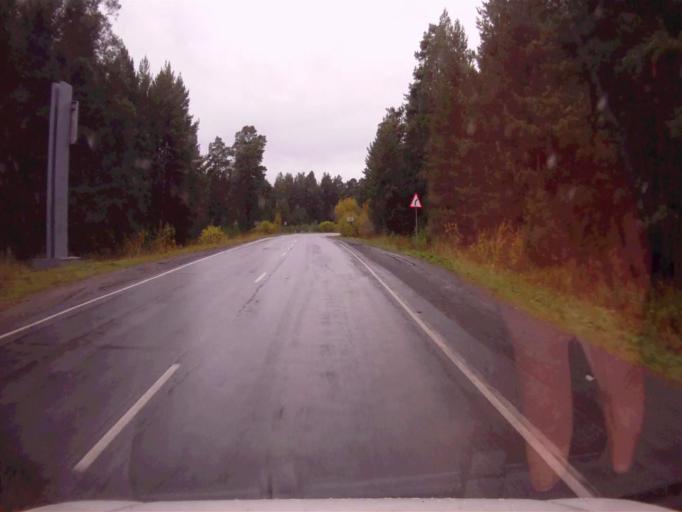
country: RU
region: Chelyabinsk
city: Verkhniy Ufaley
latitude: 56.0528
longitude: 60.1687
